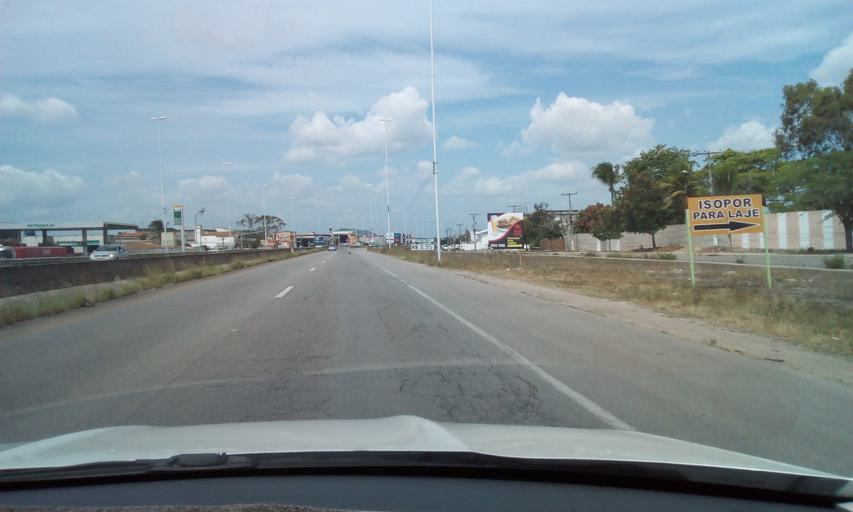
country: BR
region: Pernambuco
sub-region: Bezerros
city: Bezerros
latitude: -8.2406
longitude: -35.7488
